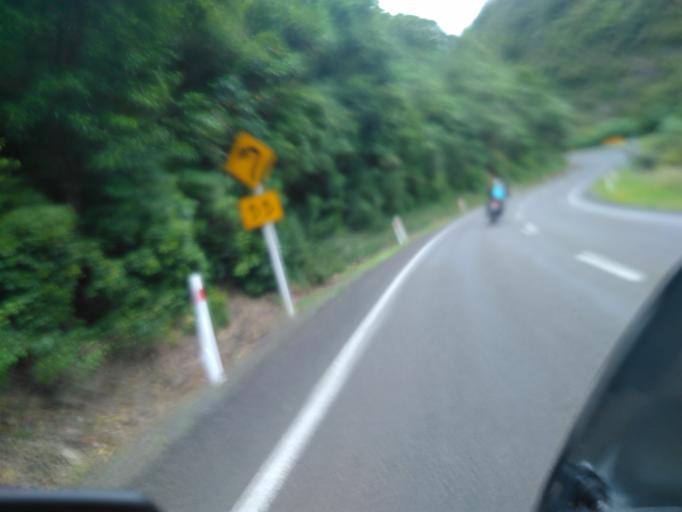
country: NZ
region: Bay of Plenty
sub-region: Opotiki District
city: Opotiki
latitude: -38.2957
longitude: 177.3912
